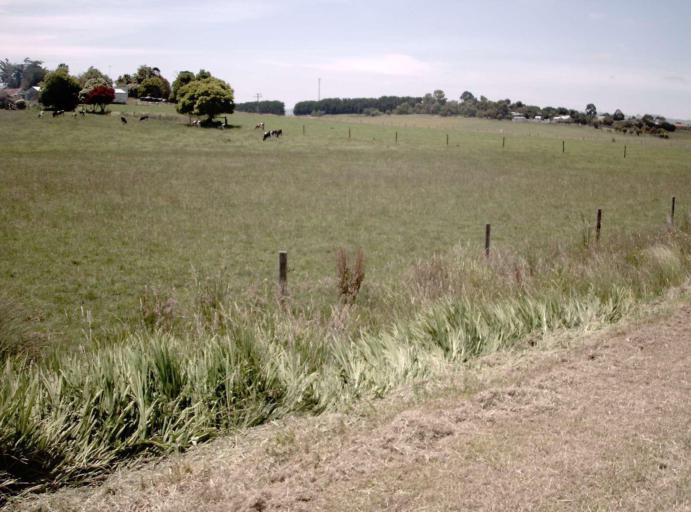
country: AU
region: Victoria
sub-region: Latrobe
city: Moe
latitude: -38.5265
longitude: 146.0859
